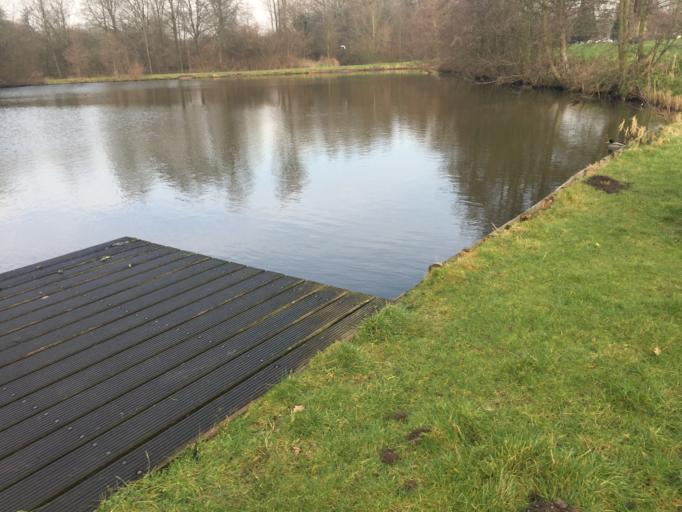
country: NL
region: Utrecht
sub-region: Gemeente Nieuwegein
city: Nieuwegein
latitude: 52.0109
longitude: 5.0817
